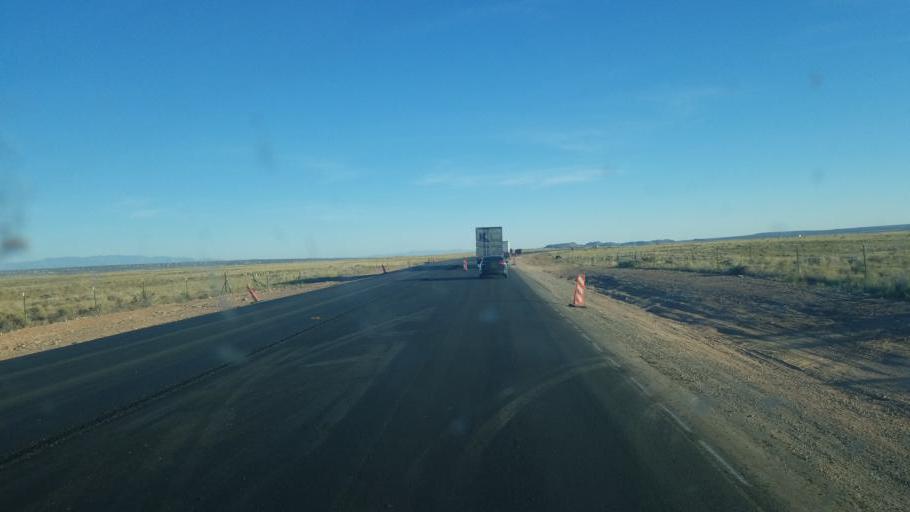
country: US
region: New Mexico
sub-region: Valencia County
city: Los Lunas
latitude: 34.8772
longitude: -107.0572
